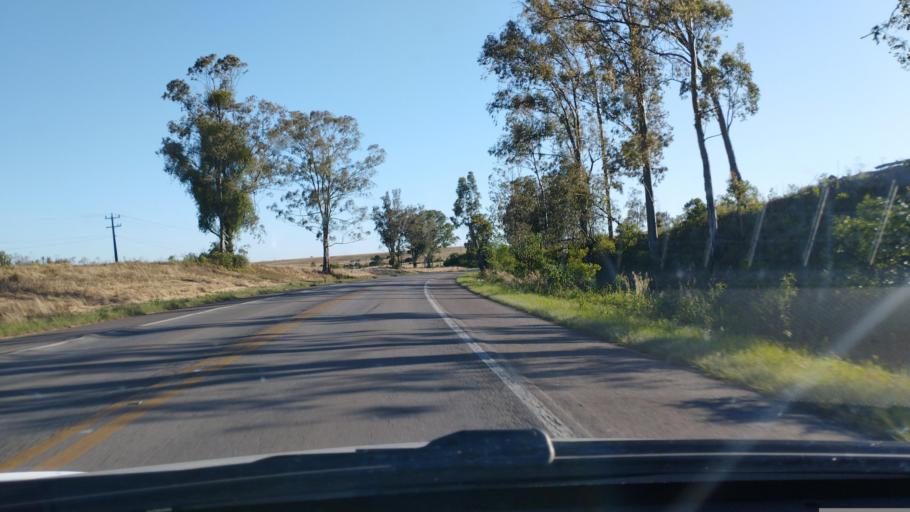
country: BR
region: Rio Grande do Sul
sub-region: Julio De Castilhos
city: Julio de Castilhos
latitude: -29.4091
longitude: -53.6680
